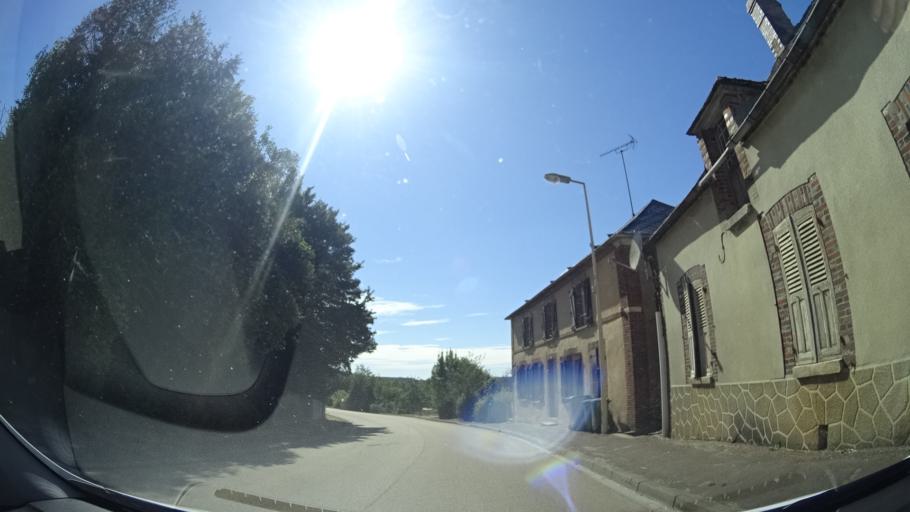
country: FR
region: Bourgogne
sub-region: Departement de l'Yonne
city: Charny
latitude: 47.9391
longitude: 3.1276
